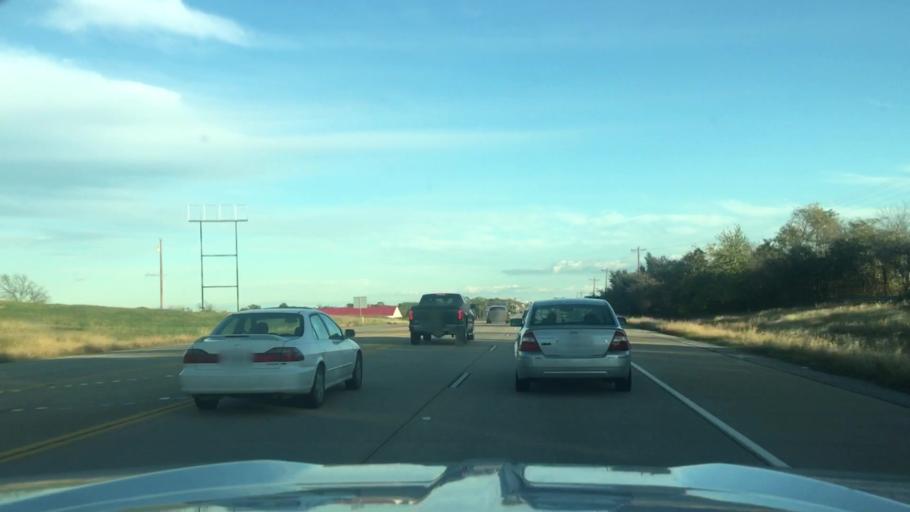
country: US
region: Texas
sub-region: Denton County
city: Cross Roads
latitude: 33.2316
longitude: -97.0054
